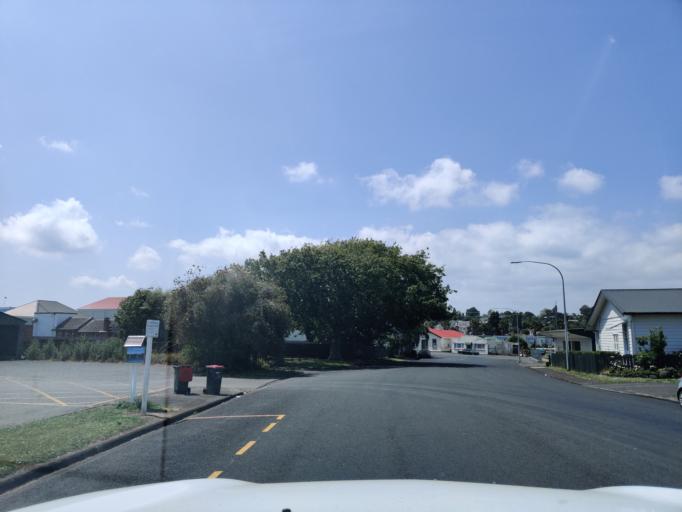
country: NZ
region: Auckland
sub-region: Auckland
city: Pukekohe East
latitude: -37.2587
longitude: 174.9475
